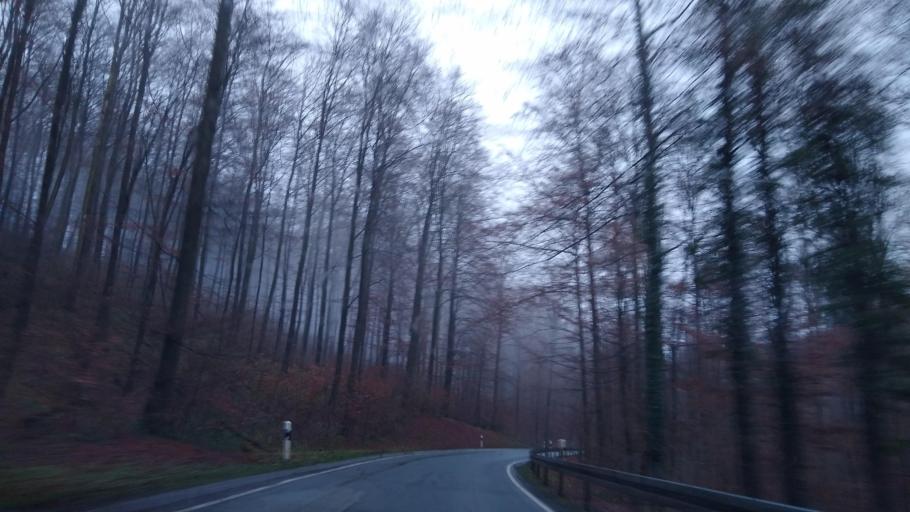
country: DE
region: Lower Saxony
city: Ottenstein
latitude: 51.9374
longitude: 9.3823
